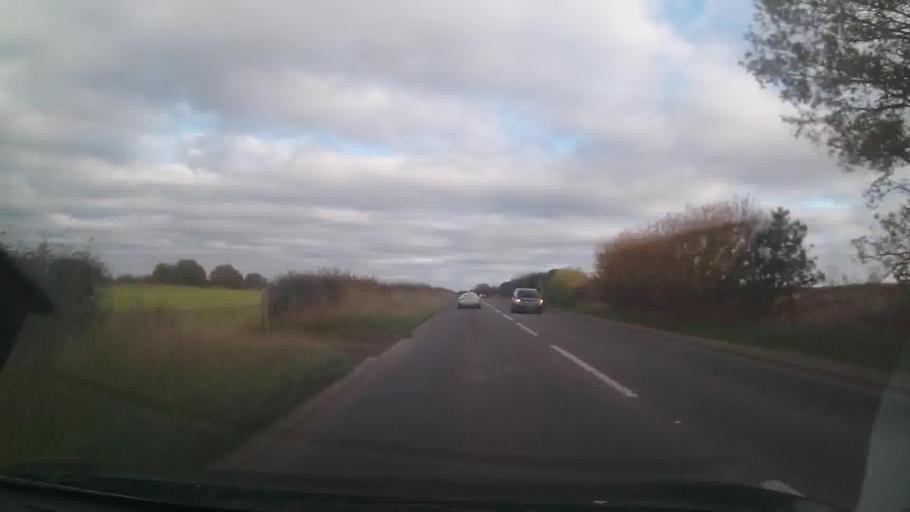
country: GB
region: England
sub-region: Shropshire
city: Stoke upon Tern
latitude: 52.8885
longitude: -2.5379
